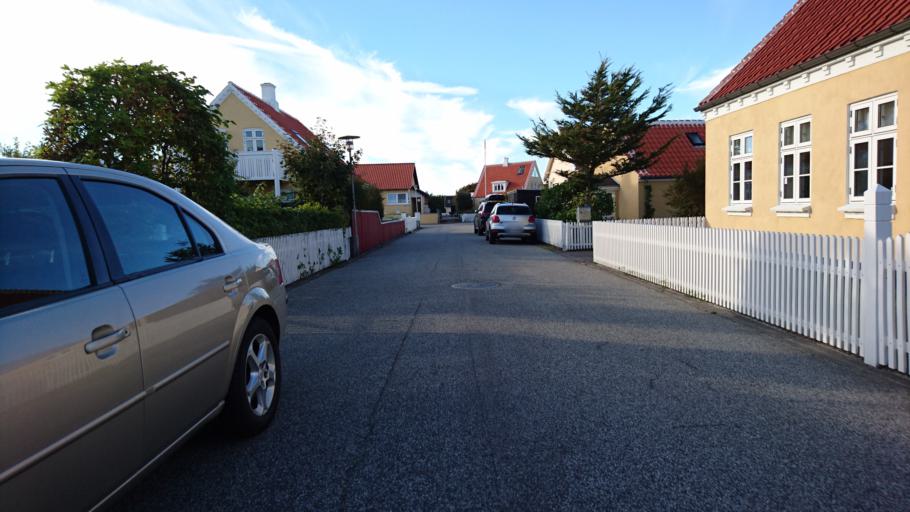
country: DK
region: North Denmark
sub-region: Frederikshavn Kommune
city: Skagen
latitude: 57.7249
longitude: 10.6023
